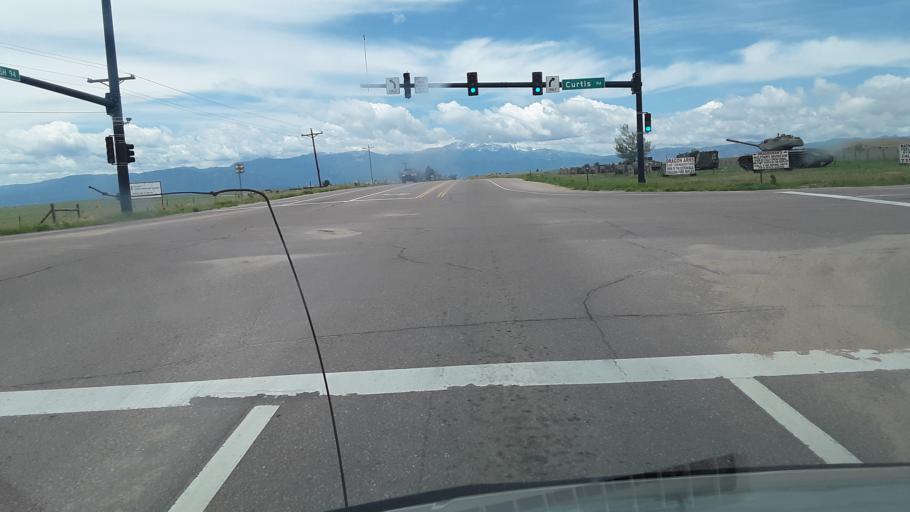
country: US
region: Colorado
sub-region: El Paso County
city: Cimarron Hills
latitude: 38.8387
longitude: -104.5532
